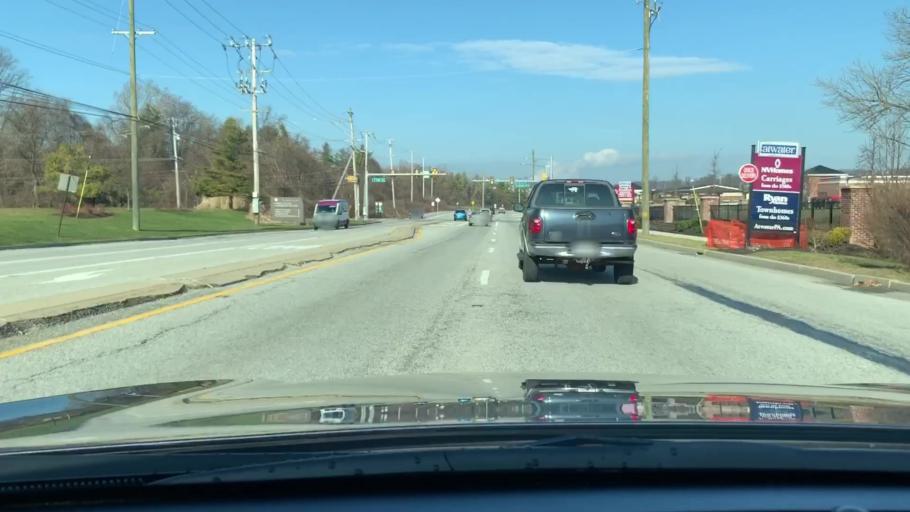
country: US
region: Pennsylvania
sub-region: Chester County
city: Malvern
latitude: 40.0653
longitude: -75.5359
